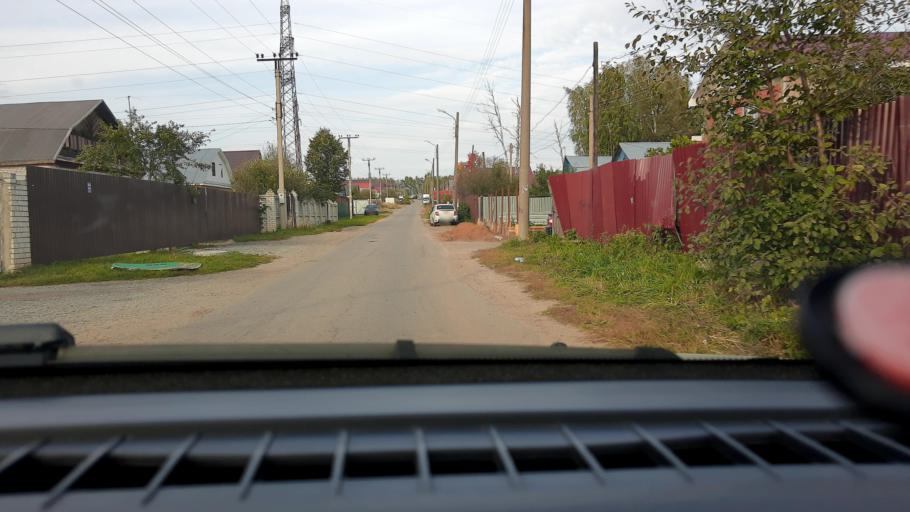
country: RU
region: Nizjnij Novgorod
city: Nizhniy Novgorod
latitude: 56.2101
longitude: 43.9556
